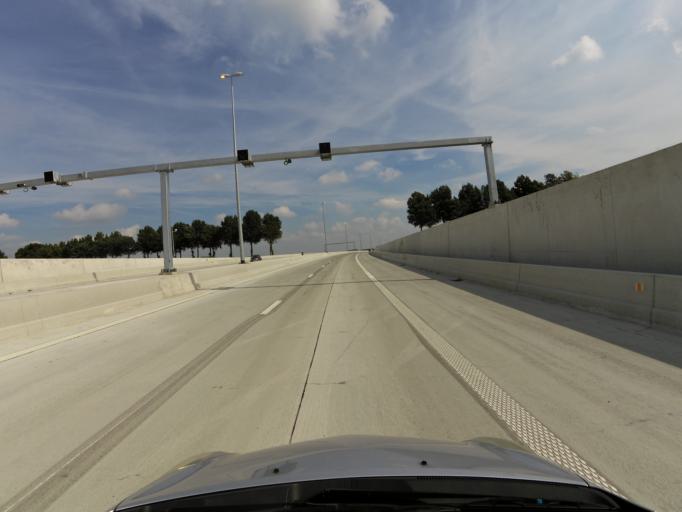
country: BE
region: Flanders
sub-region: Provincie West-Vlaanderen
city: Knokke-Heist
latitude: 51.3072
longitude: 3.3050
